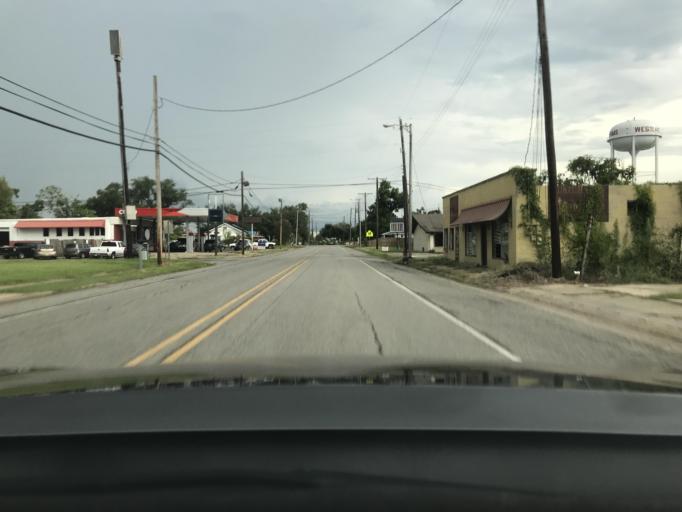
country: US
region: Louisiana
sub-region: Calcasieu Parish
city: Westlake
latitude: 30.2407
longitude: -93.2505
